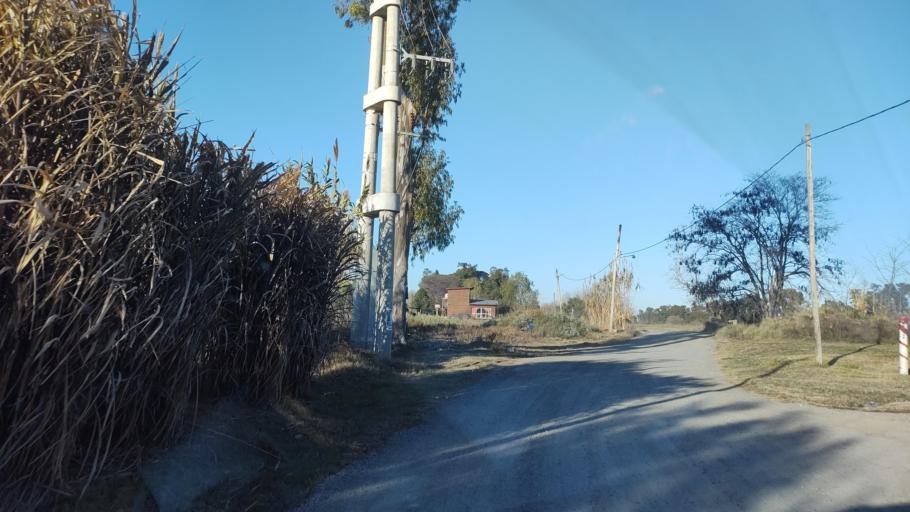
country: AR
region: Buenos Aires
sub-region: Partido de La Plata
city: La Plata
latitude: -34.9056
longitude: -58.0523
